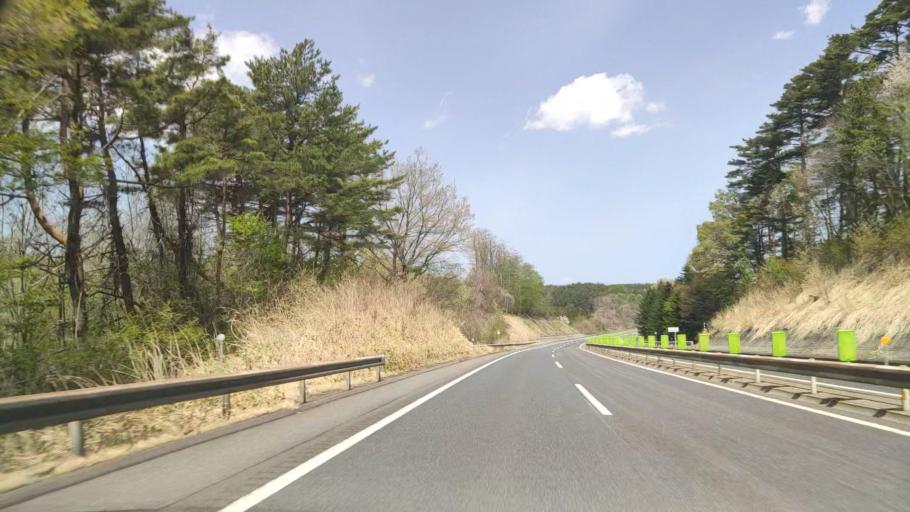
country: JP
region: Aomori
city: Hachinohe
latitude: 40.4190
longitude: 141.4400
